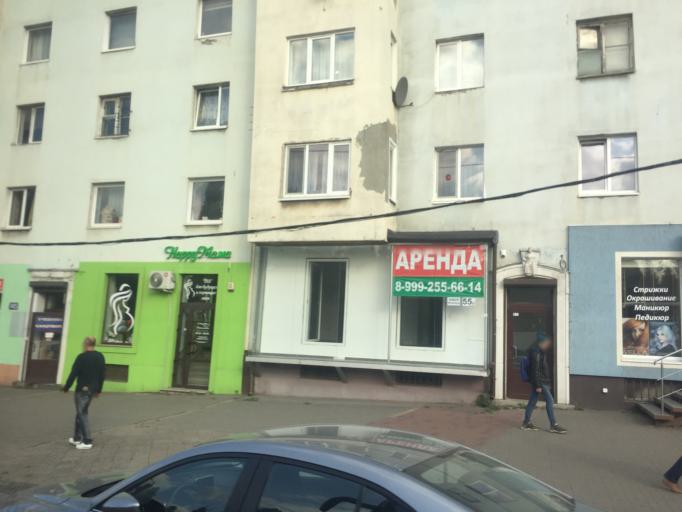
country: RU
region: Kaliningrad
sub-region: Gorod Kaliningrad
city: Kaliningrad
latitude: 54.6975
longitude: 20.5029
